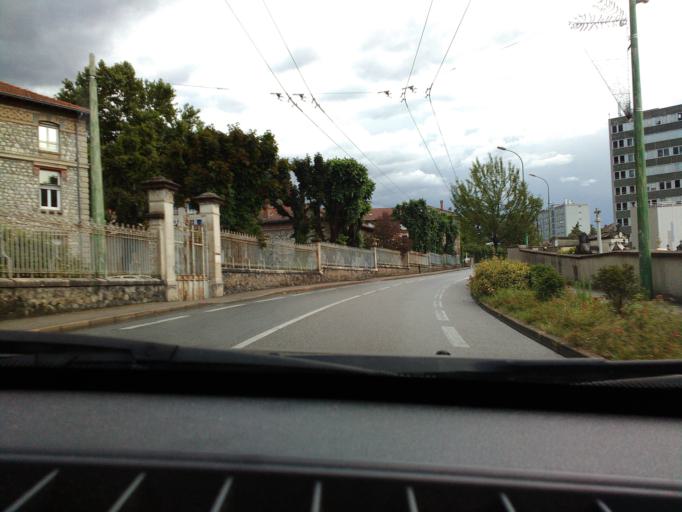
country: FR
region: Rhone-Alpes
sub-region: Departement de l'Isere
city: La Tronche
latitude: 45.2018
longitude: 5.7427
